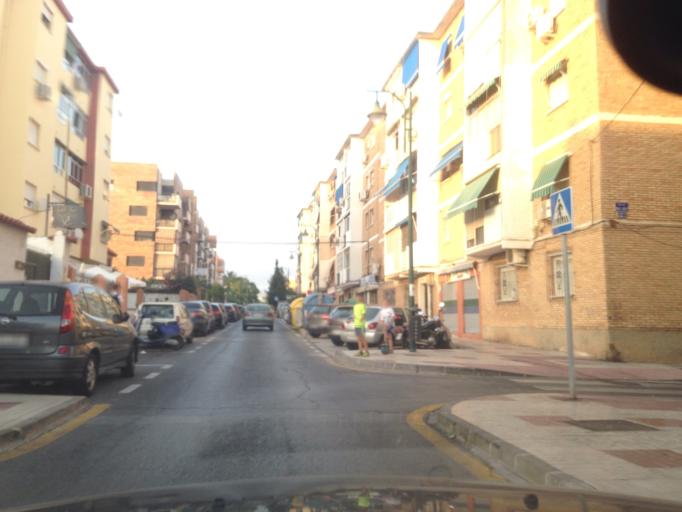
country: ES
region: Andalusia
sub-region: Provincia de Malaga
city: Malaga
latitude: 36.7204
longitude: -4.4542
